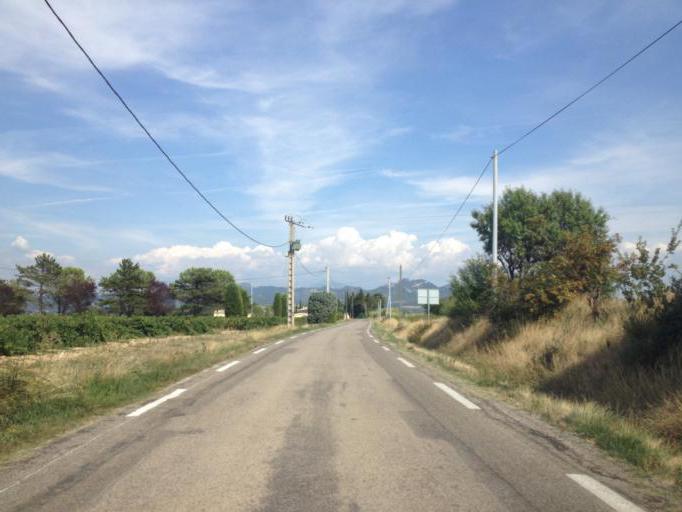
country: FR
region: Provence-Alpes-Cote d'Azur
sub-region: Departement du Vaucluse
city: Violes
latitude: 44.1607
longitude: 4.9171
